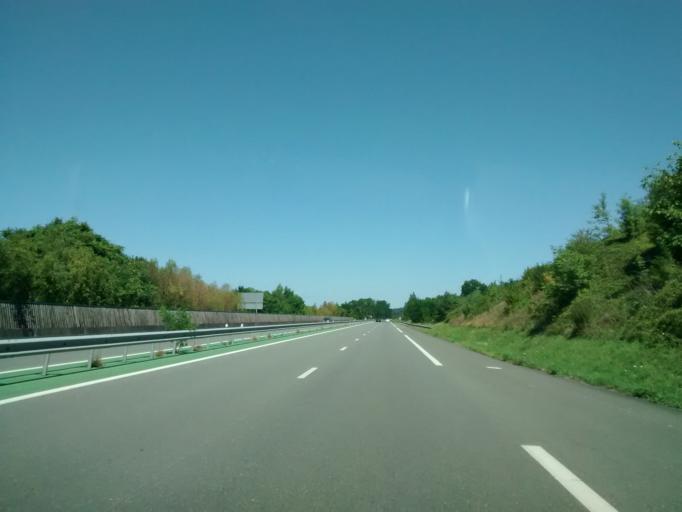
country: FR
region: Aquitaine
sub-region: Departement de la Dordogne
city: Neuvic
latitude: 45.0756
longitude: 0.4493
